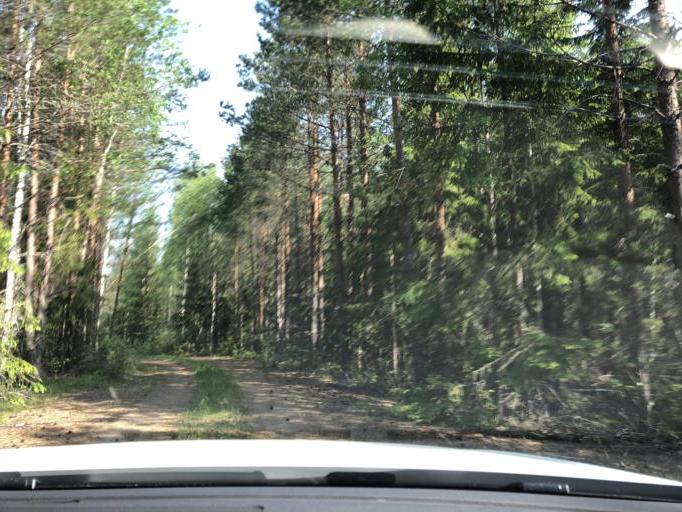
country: SE
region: Dalarna
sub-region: Avesta Kommun
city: Horndal
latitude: 60.2199
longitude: 16.5176
